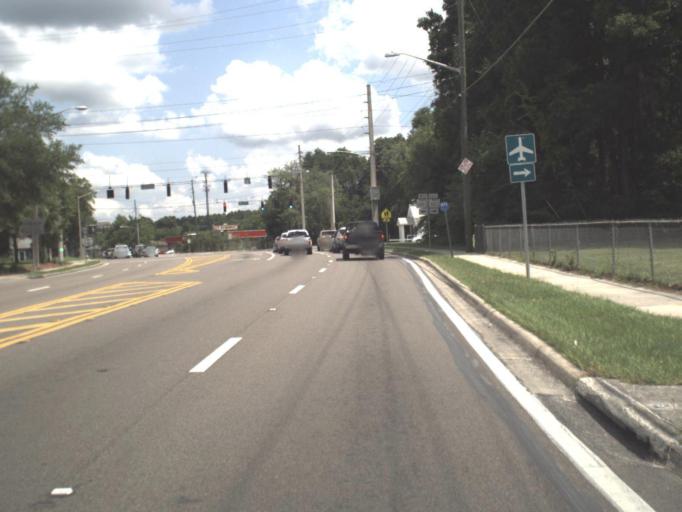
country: US
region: Florida
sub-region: Alachua County
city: Gainesville
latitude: 29.6875
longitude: -82.3307
